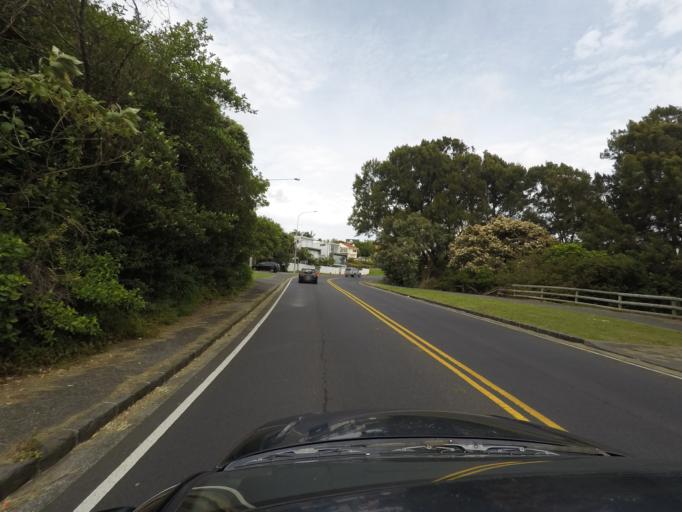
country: NZ
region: Auckland
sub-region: Auckland
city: Auckland
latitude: -36.8556
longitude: 174.8096
